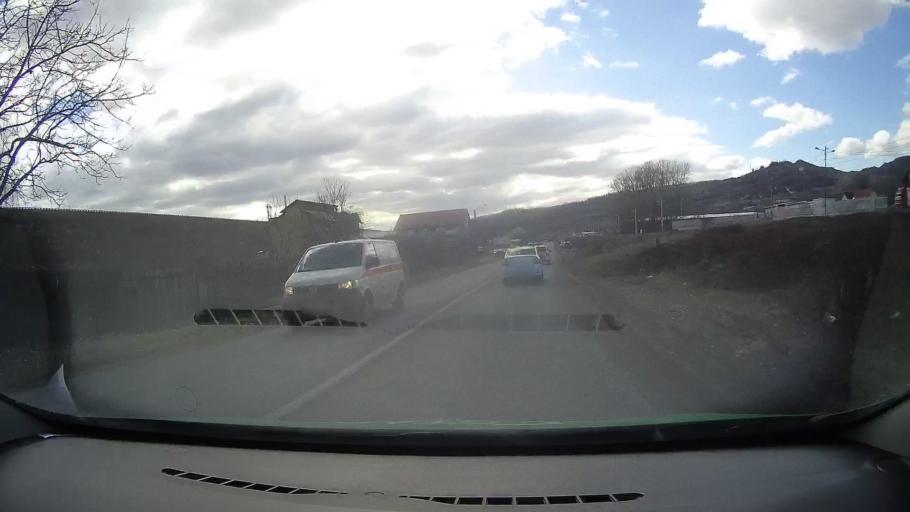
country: RO
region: Dambovita
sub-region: Comuna Motaeni
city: Motaeni
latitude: 45.0891
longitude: 25.4227
